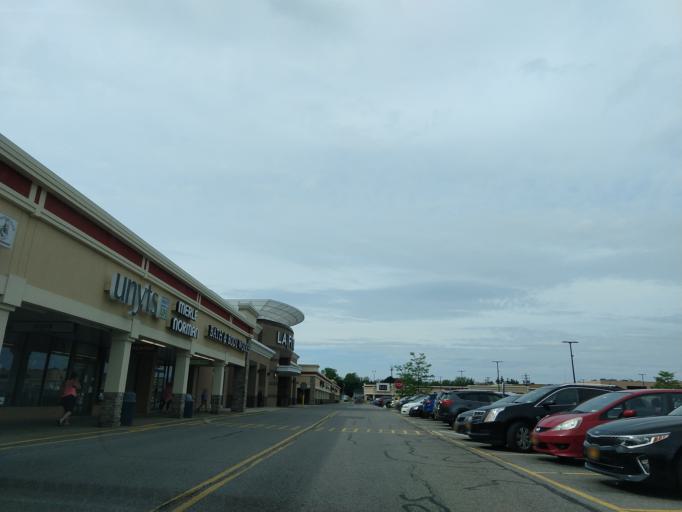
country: US
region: New York
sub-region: Erie County
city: West Seneca
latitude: 42.8267
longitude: -78.7558
